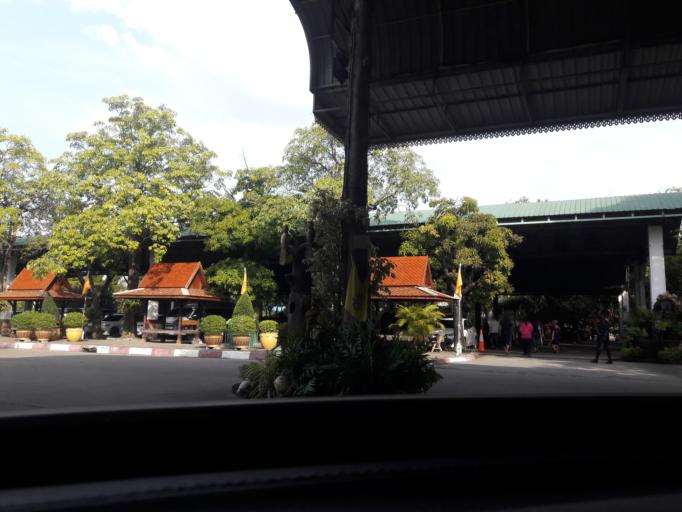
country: TH
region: Sing Buri
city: Sing Buri
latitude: 14.8517
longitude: 100.3884
